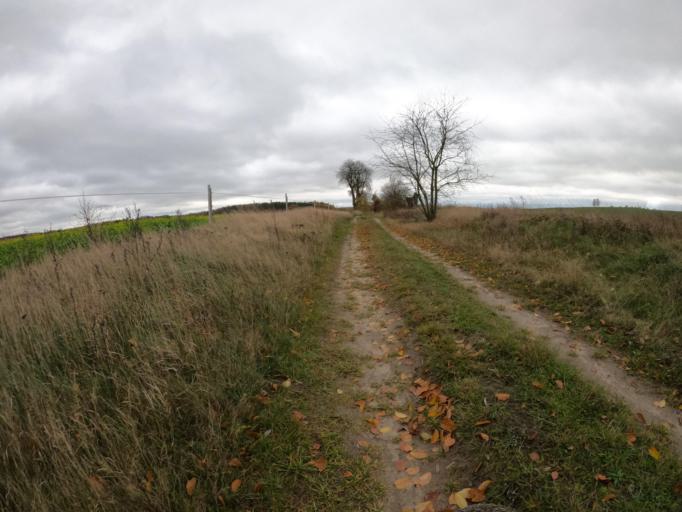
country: PL
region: West Pomeranian Voivodeship
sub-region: Powiat walecki
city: Tuczno
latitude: 53.2462
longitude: 16.2076
